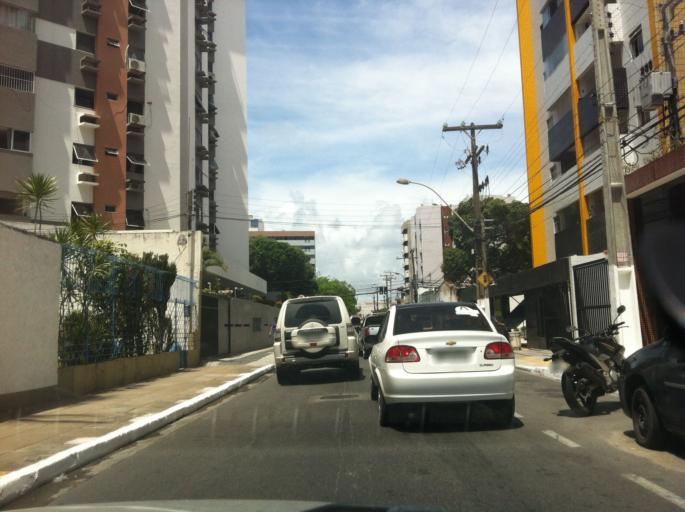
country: BR
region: Alagoas
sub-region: Maceio
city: Maceio
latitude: -9.6621
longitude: -35.7082
